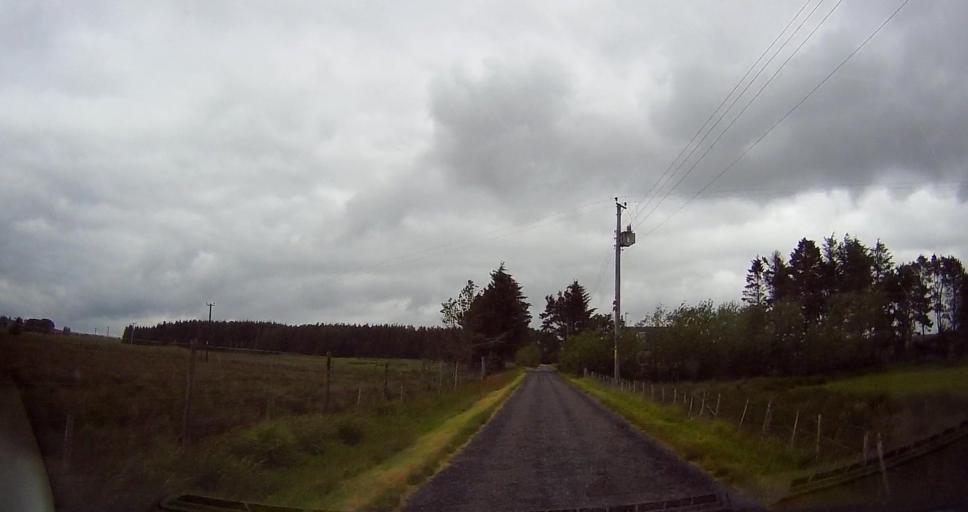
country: GB
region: Scotland
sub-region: Highland
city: Alness
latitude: 58.0644
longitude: -4.4267
